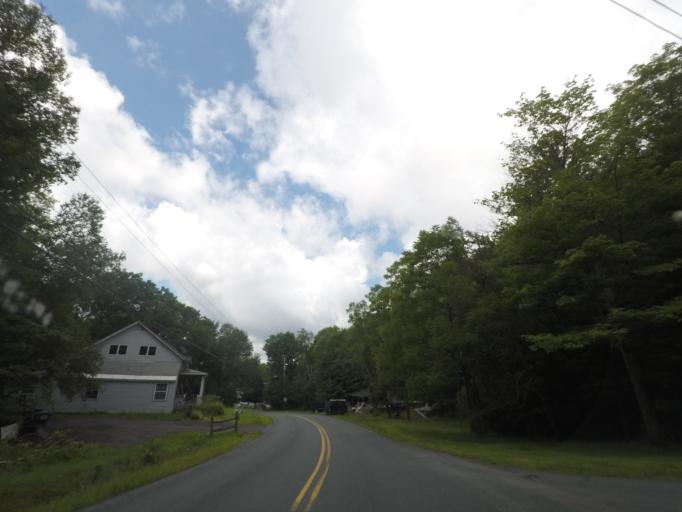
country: US
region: New York
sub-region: Rensselaer County
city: Averill Park
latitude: 42.6432
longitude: -73.4745
